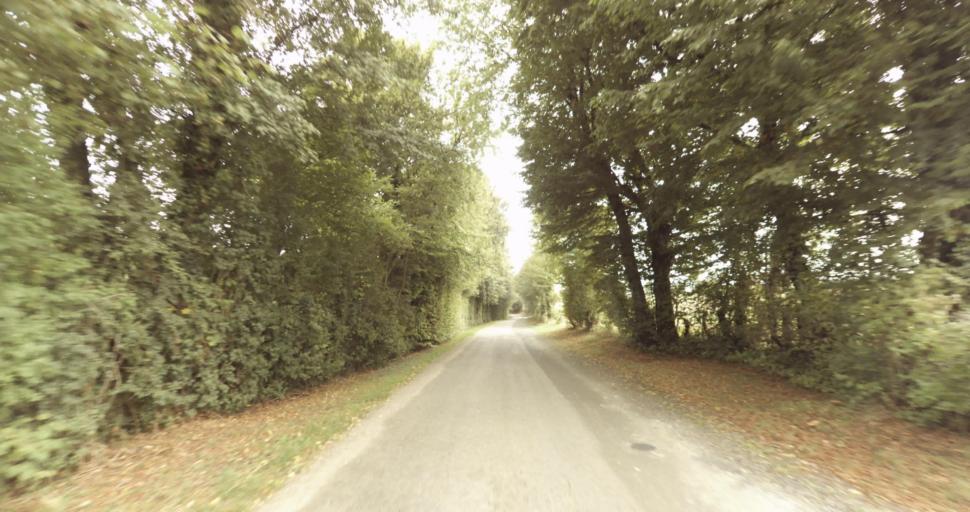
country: FR
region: Lower Normandy
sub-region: Departement de l'Orne
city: Sainte-Gauburge-Sainte-Colombe
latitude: 48.7391
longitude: 0.3661
